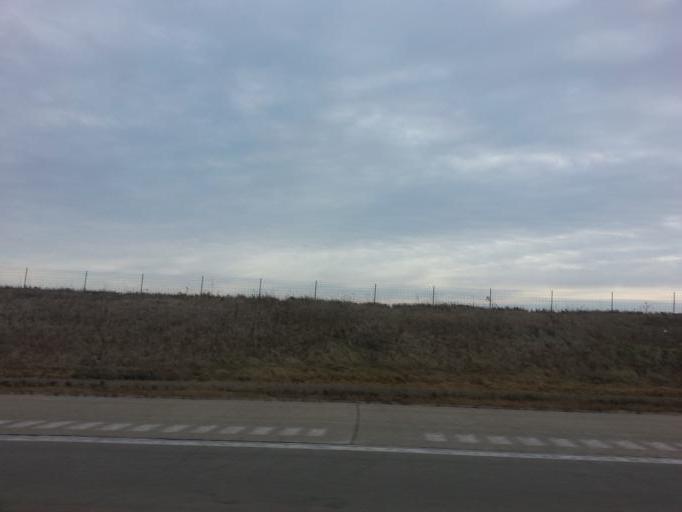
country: US
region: Illinois
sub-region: Woodford County
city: El Paso
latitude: 40.7924
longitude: -89.0352
